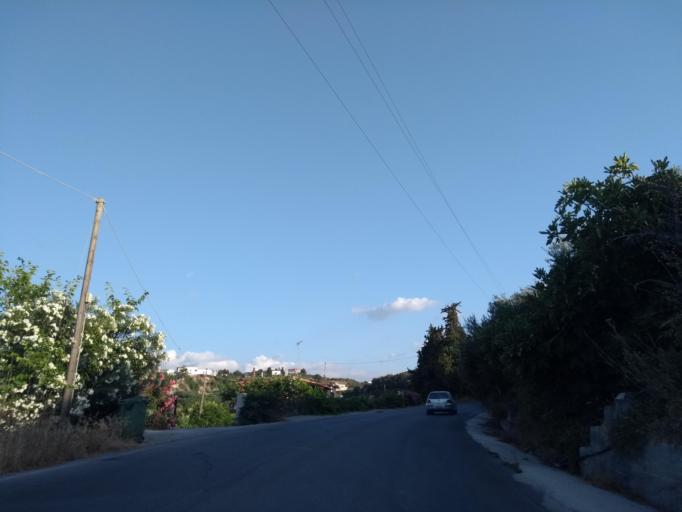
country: GR
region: Crete
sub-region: Nomos Chanias
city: Kalivai
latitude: 35.4382
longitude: 24.1757
